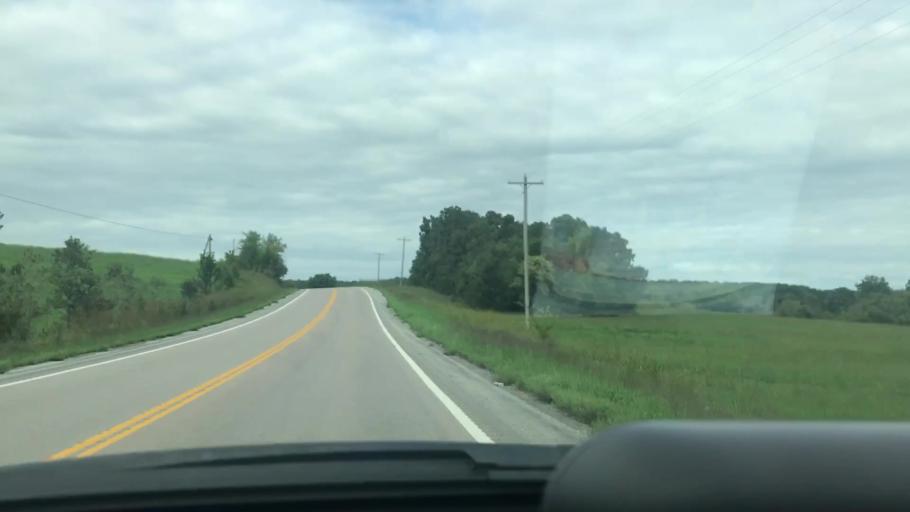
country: US
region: Missouri
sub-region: Benton County
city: Warsaw
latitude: 38.1297
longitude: -93.2802
